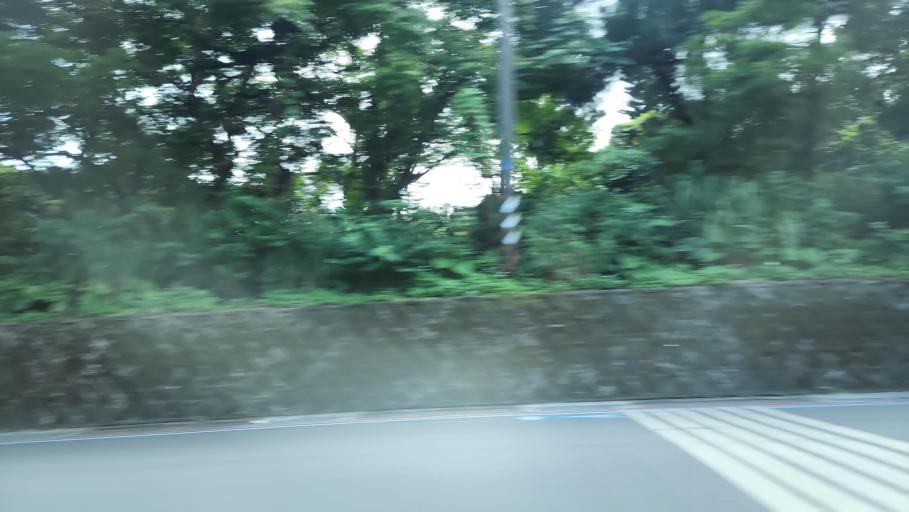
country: TW
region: Taiwan
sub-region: Keelung
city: Keelung
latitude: 25.2231
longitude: 121.6443
